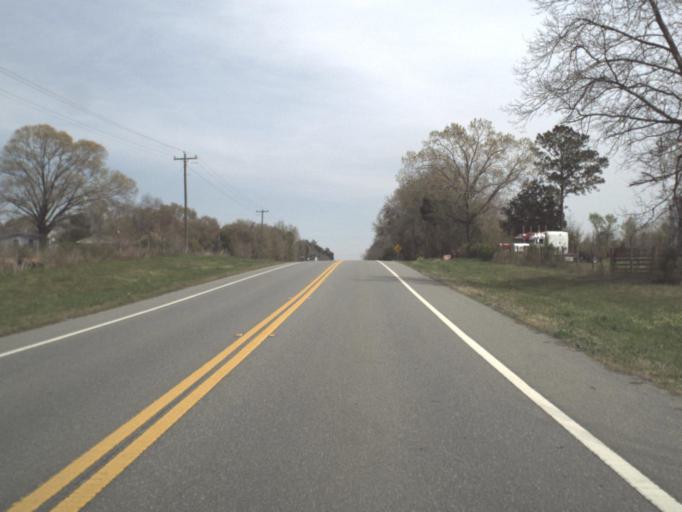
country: US
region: Alabama
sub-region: Geneva County
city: Hartford
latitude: 30.9591
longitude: -85.6713
